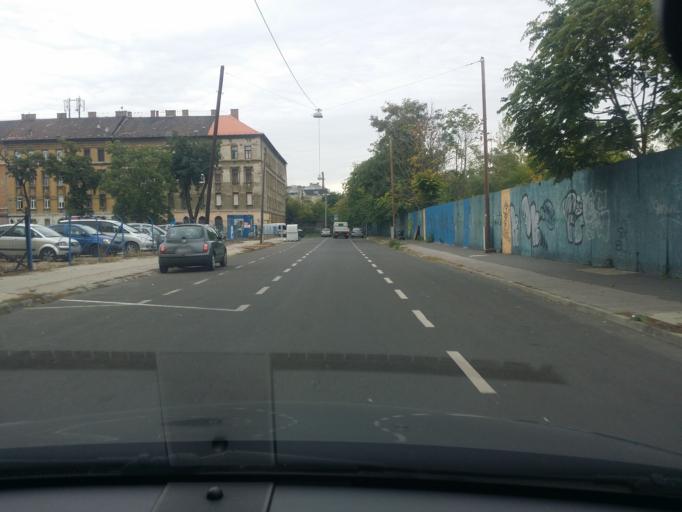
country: HU
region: Budapest
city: Budapest VI. keruelet
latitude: 47.5172
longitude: 19.0647
